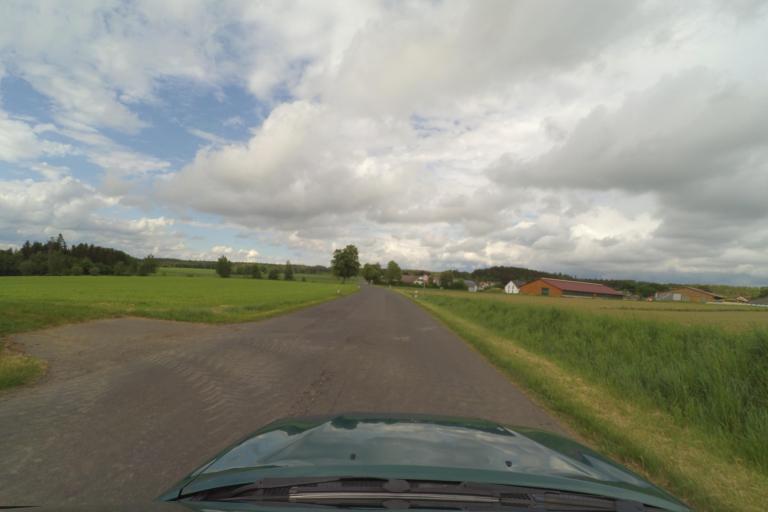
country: DE
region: Bavaria
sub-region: Upper Palatinate
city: Schwarzenbach
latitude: 49.8407
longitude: 12.3752
